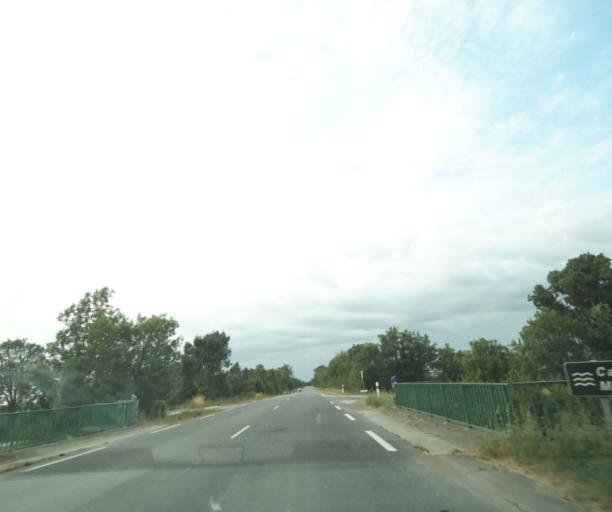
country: FR
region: Poitou-Charentes
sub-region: Departement de la Charente-Maritime
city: Marans
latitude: 46.3322
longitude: -0.9964
